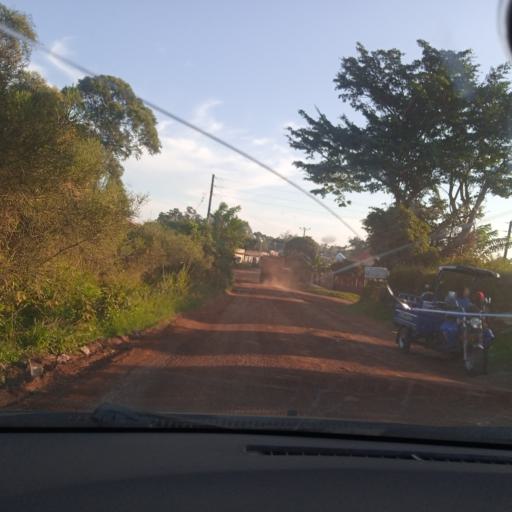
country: UG
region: Central Region
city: Masaka
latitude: -0.3415
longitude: 31.7616
